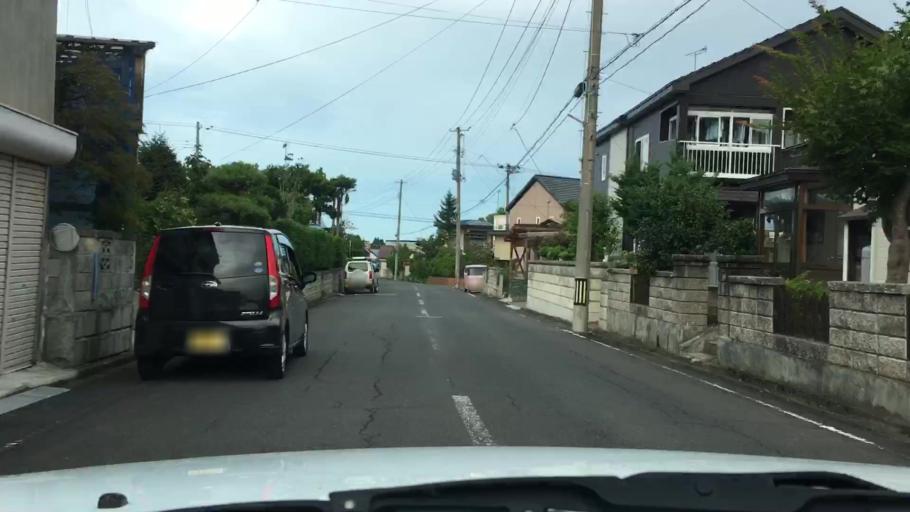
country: JP
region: Aomori
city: Hirosaki
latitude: 40.5730
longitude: 140.4520
